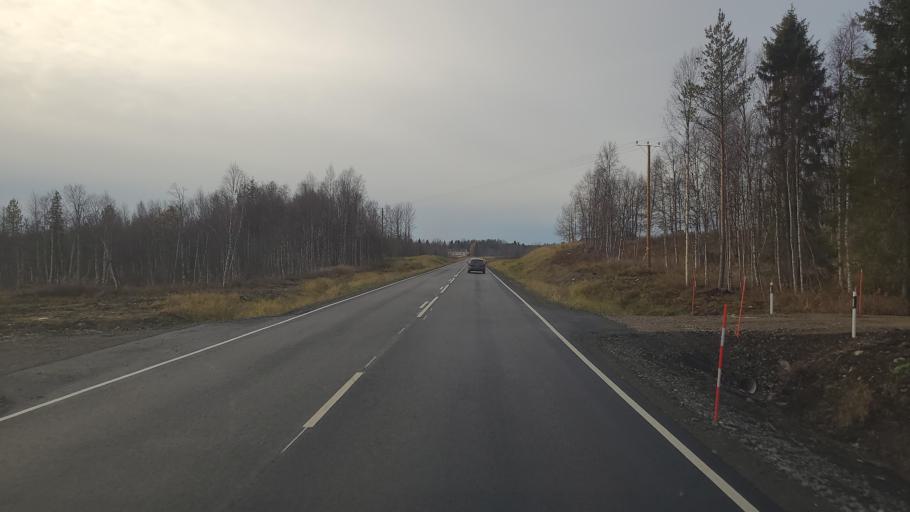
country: FI
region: Lapland
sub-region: Tunturi-Lappi
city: Kittilae
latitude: 67.8649
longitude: 24.9565
